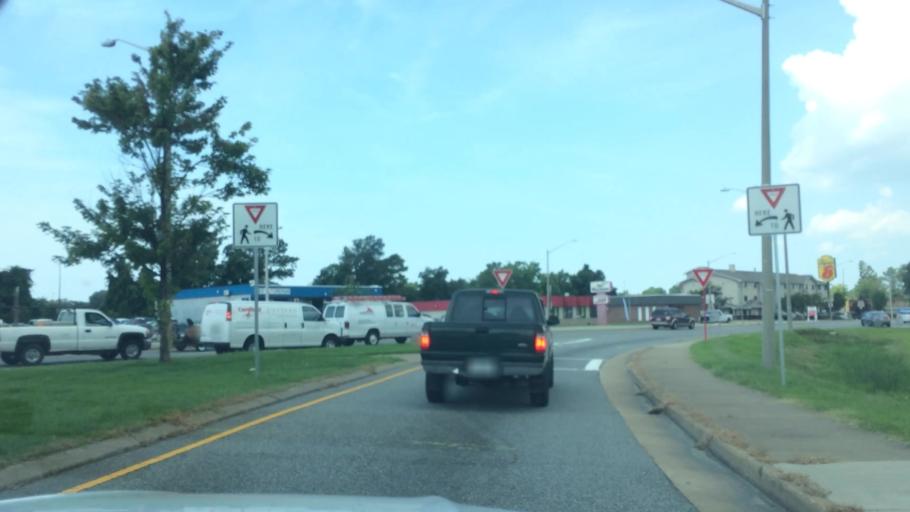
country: US
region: Virginia
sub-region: City of Newport News
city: Newport News
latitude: 37.0202
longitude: -76.4445
